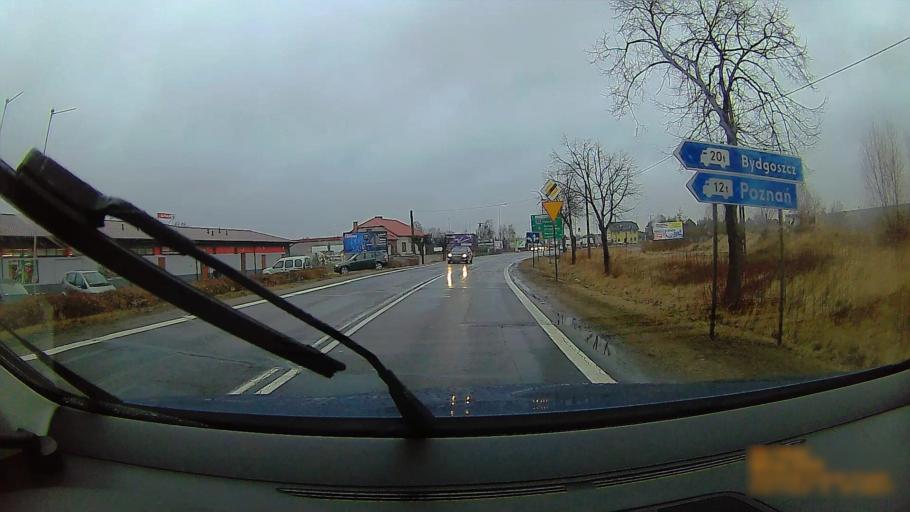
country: PL
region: Greater Poland Voivodeship
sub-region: Konin
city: Konin
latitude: 52.1902
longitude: 18.2647
